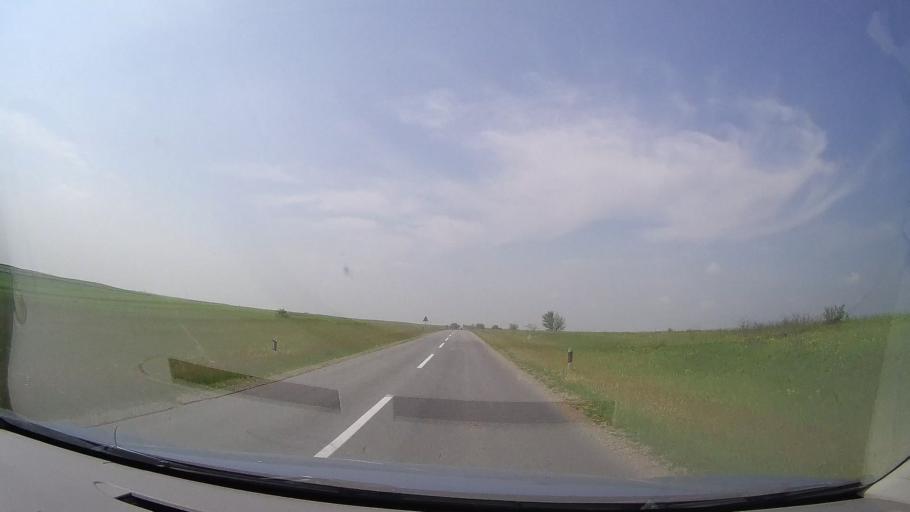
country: RS
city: Samos
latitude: 45.1755
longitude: 20.7580
